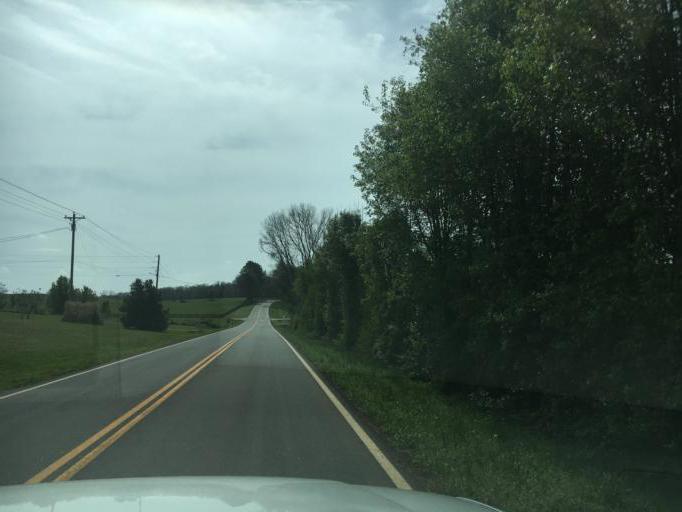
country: US
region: Georgia
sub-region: Franklin County
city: Lavonia
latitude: 34.3885
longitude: -83.0601
